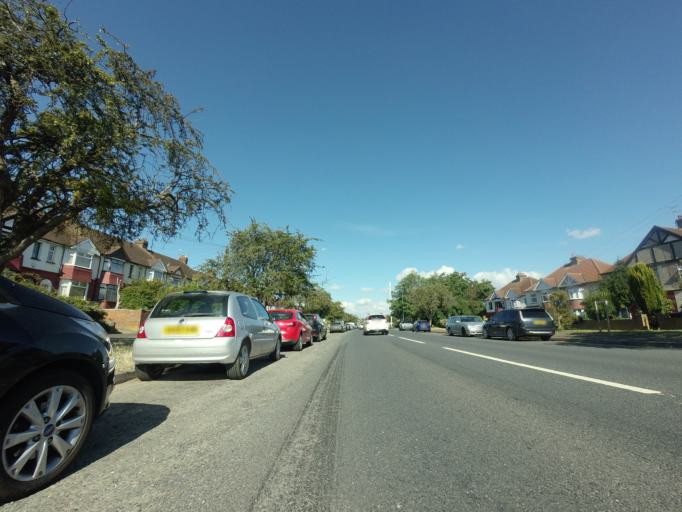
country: GB
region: England
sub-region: Kent
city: Gravesend
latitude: 51.4305
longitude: 0.3985
